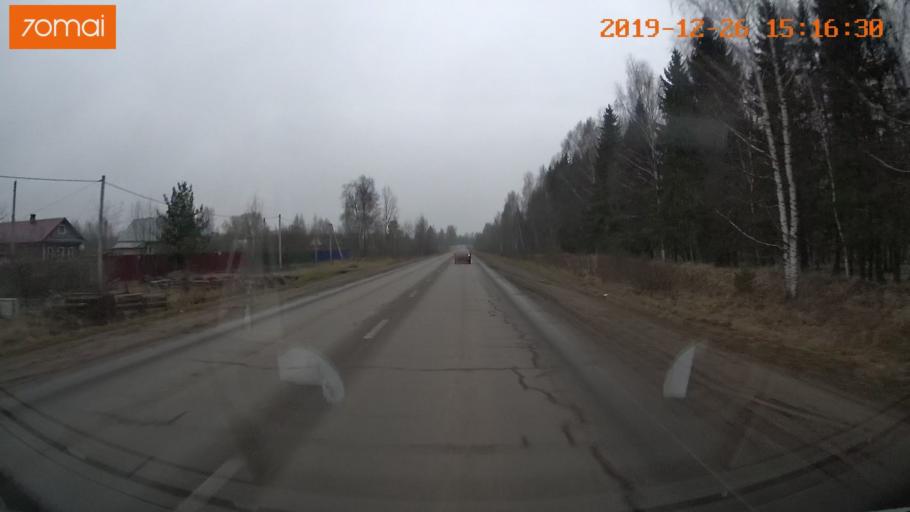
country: RU
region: Jaroslavl
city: Rybinsk
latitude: 58.0857
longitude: 38.8646
